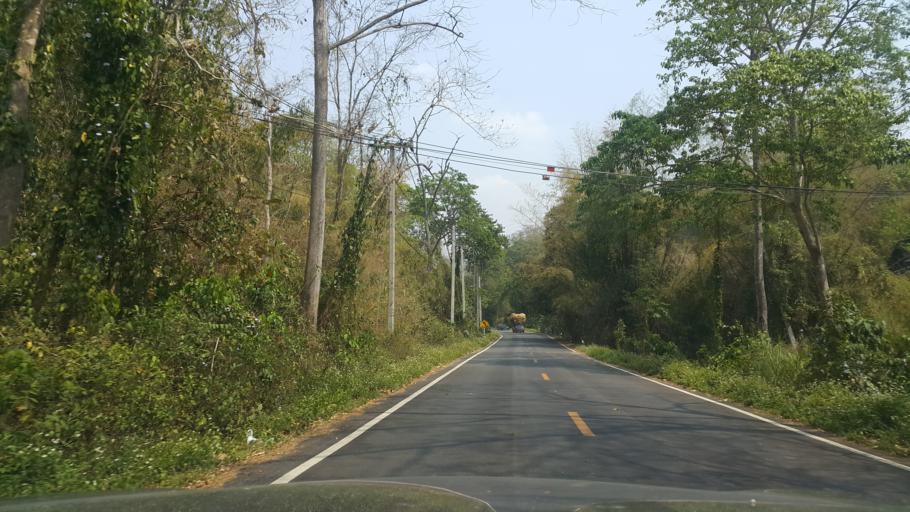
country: TH
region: Lamphun
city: Thung Hua Chang
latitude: 17.9016
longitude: 99.1309
